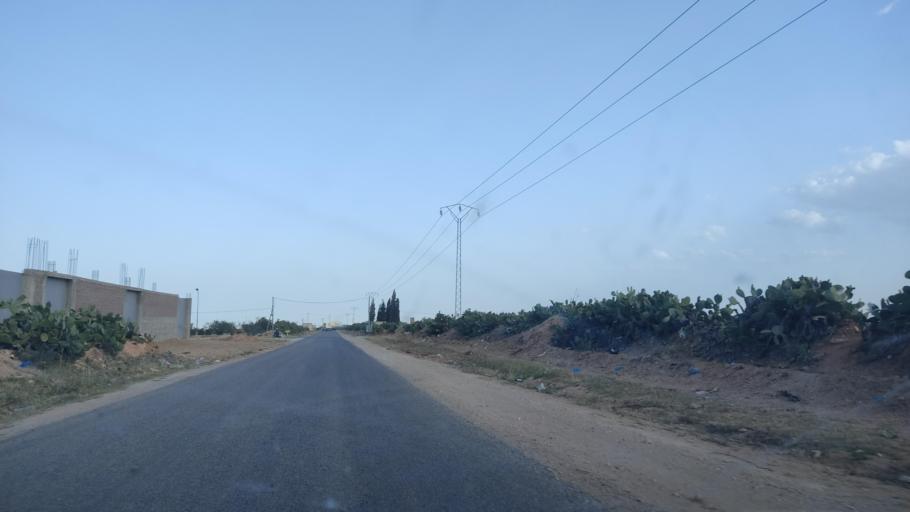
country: TN
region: Safaqis
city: Sfax
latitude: 34.8160
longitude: 10.6556
